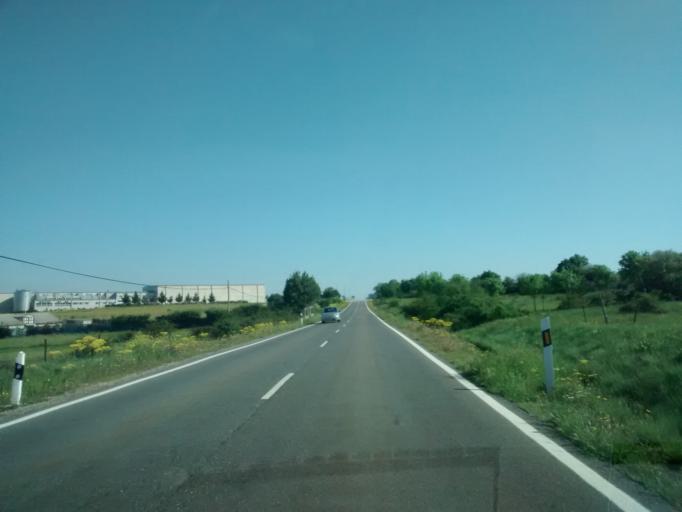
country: ES
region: Castille and Leon
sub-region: Provincia de Segovia
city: Trescasas
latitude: 40.9468
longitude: -4.0339
